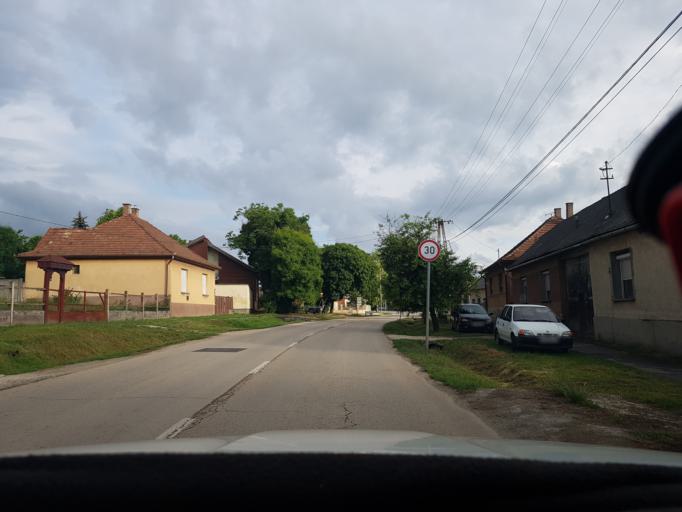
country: HU
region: Komarom-Esztergom
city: Sarisap
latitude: 47.6772
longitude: 18.6793
